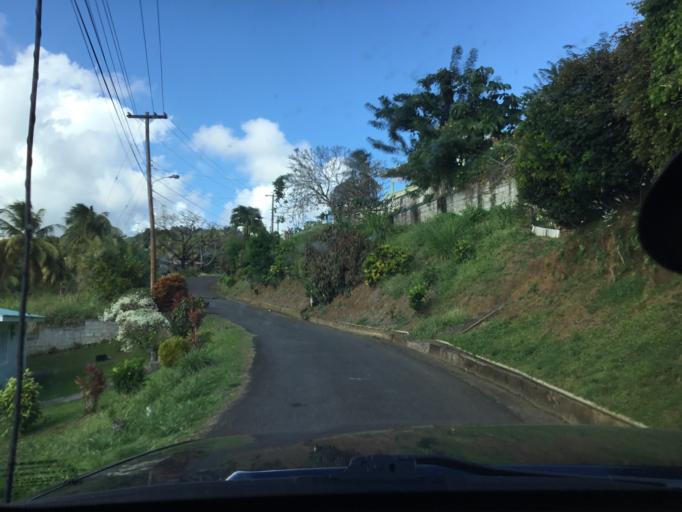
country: VC
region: Saint George
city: Kingstown
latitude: 13.1536
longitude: -61.1780
